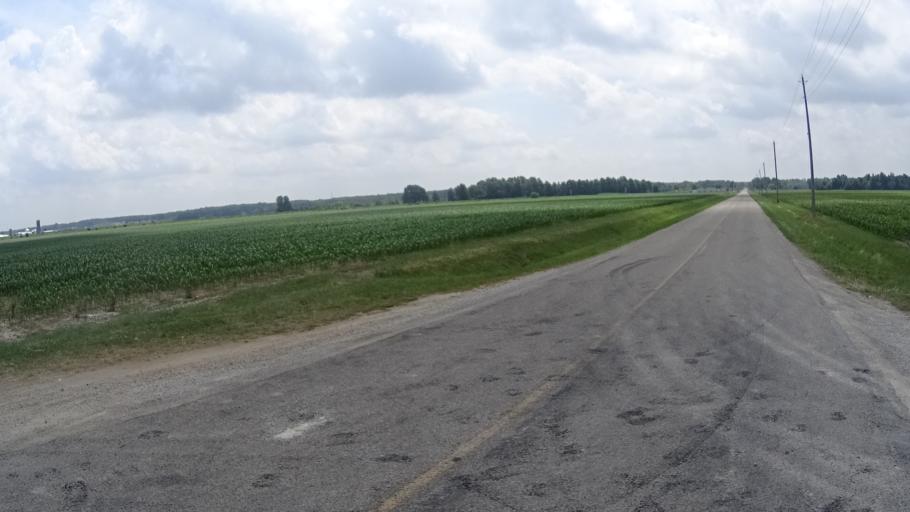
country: US
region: Ohio
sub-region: Lorain County
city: Vermilion
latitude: 41.4100
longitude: -82.3905
